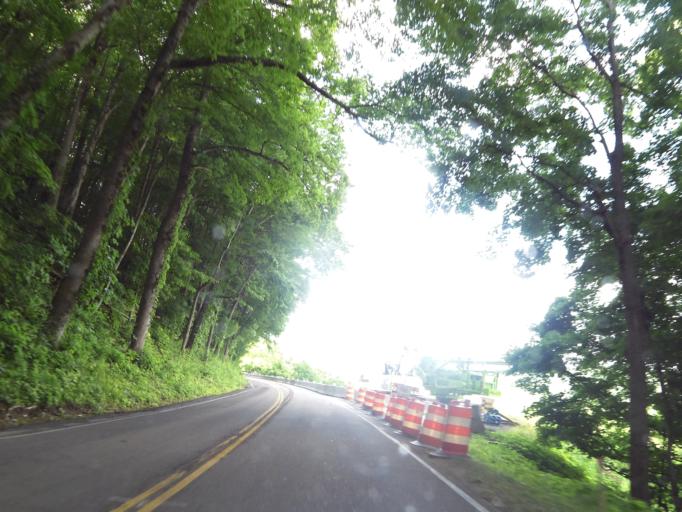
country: US
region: Tennessee
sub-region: Sevier County
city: Gatlinburg
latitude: 35.6599
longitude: -83.5208
